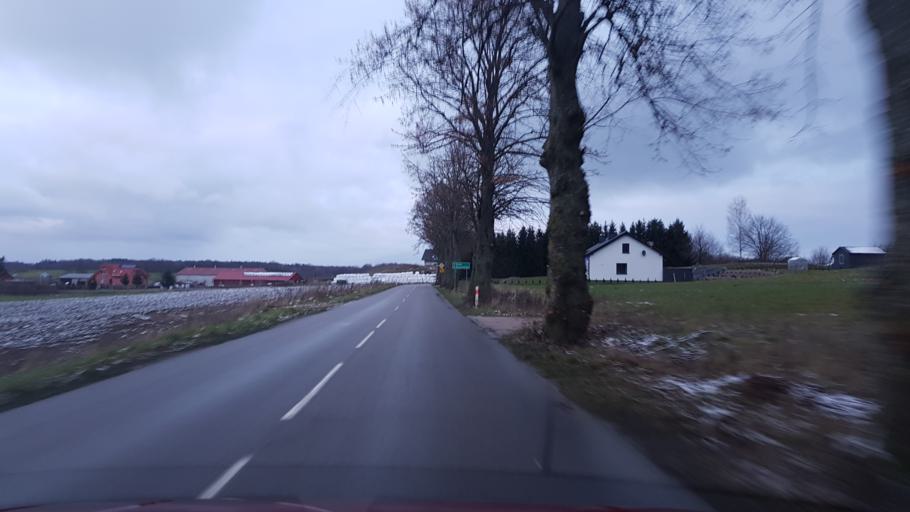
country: PL
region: Pomeranian Voivodeship
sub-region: Powiat bytowski
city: Tuchomie
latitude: 54.1213
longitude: 17.3375
